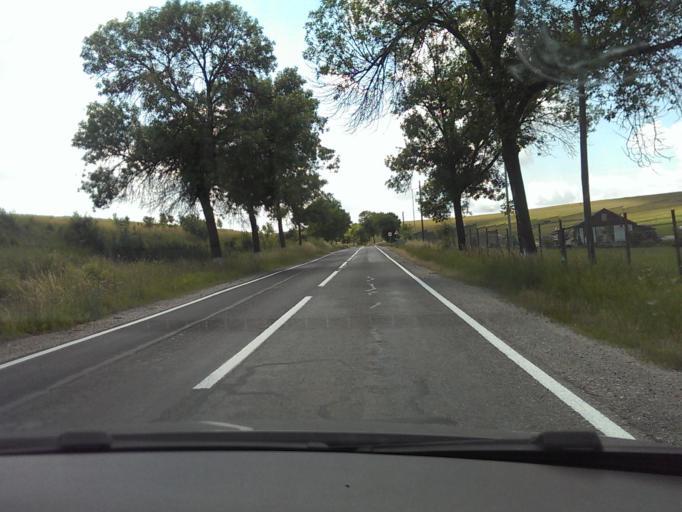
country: RO
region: Cluj
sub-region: Comuna Apahida
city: Apahida
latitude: 46.8077
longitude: 23.7780
